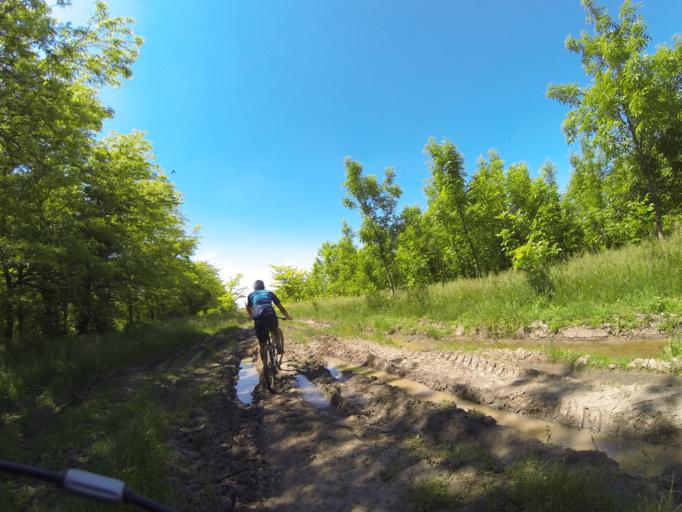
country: RO
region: Dolj
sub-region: Comuna Leu
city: Leu
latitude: 44.2018
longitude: 24.0345
